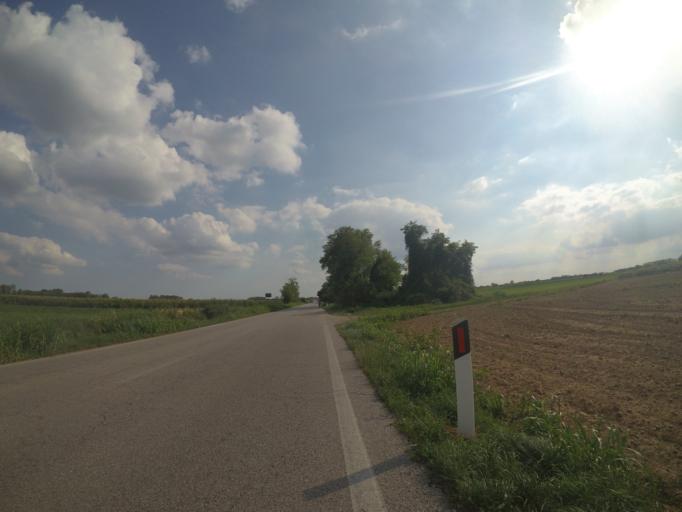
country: IT
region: Friuli Venezia Giulia
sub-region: Provincia di Udine
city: Fagagna
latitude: 46.0956
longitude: 13.0915
